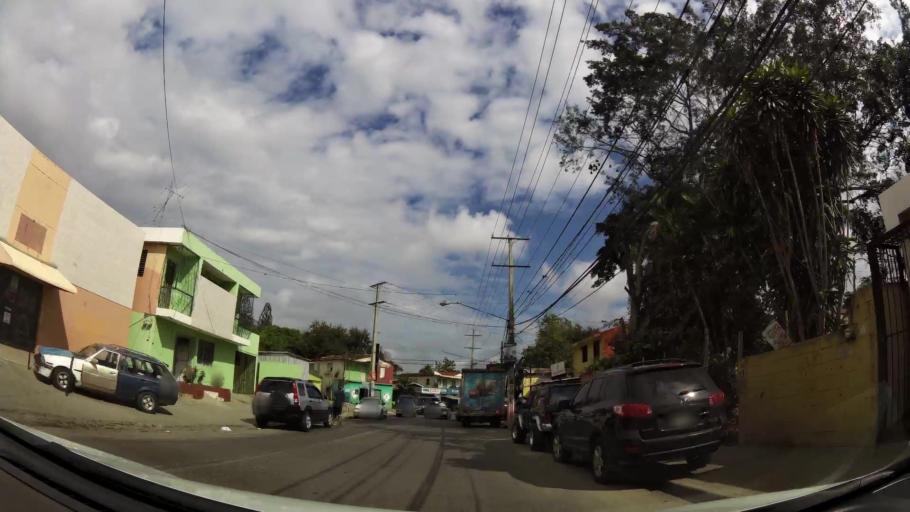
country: DO
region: Santiago
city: Santiago de los Caballeros
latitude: 19.4424
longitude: -70.7074
